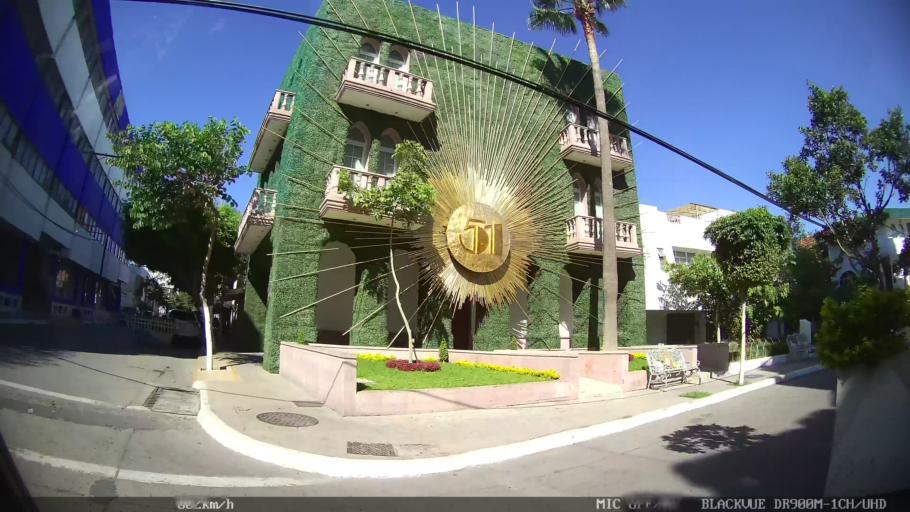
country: MX
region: Jalisco
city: Tlaquepaque
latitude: 20.6720
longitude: -103.2840
